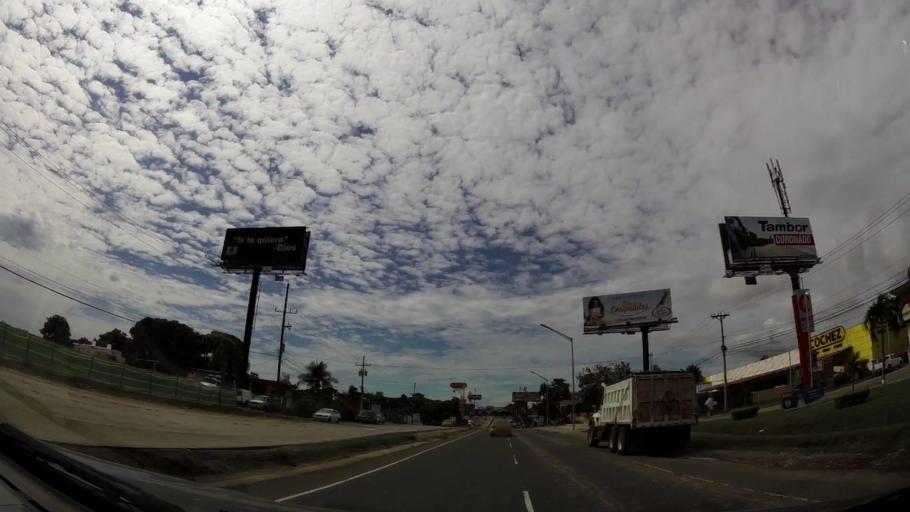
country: PA
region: Panama
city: Nueva Gorgona
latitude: 8.5458
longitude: -79.9123
